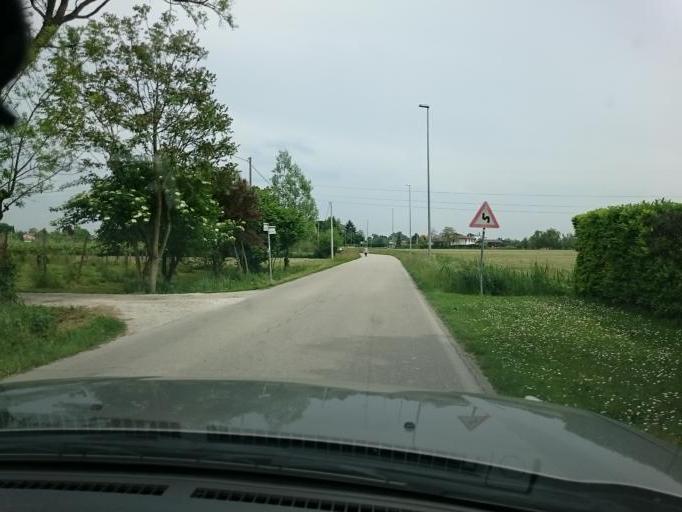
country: IT
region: Veneto
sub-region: Provincia di Venezia
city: Fiesso
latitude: 45.4137
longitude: 12.0356
